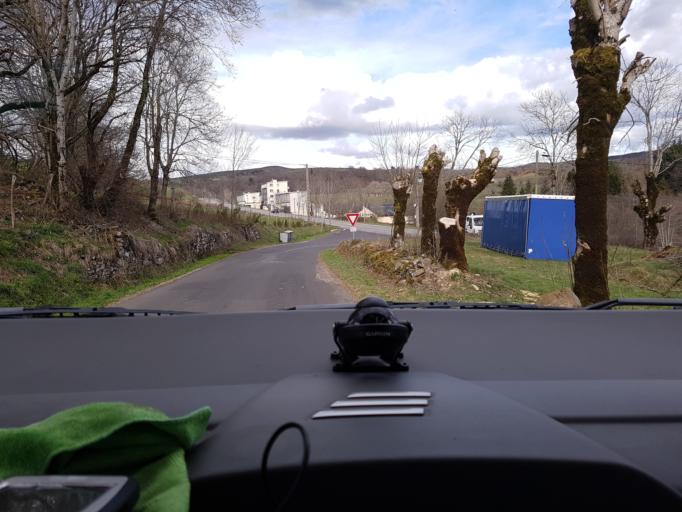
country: FR
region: Midi-Pyrenees
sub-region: Departement de l'Aveyron
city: Laguiole
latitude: 44.6896
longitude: 2.8555
